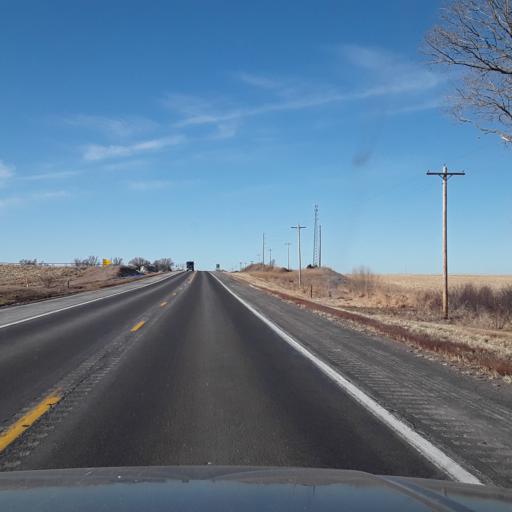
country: US
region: Nebraska
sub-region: Adams County
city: Hastings
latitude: 40.5681
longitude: -98.4982
